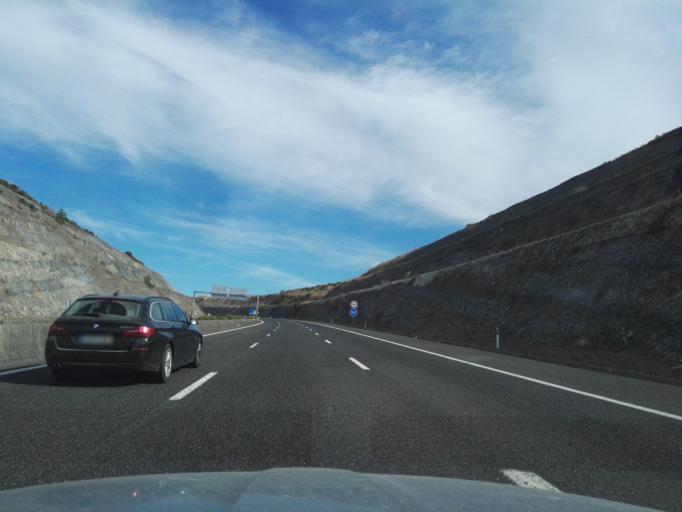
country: PT
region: Lisbon
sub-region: Vila Franca de Xira
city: Vialonga
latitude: 38.9126
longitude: -9.0724
